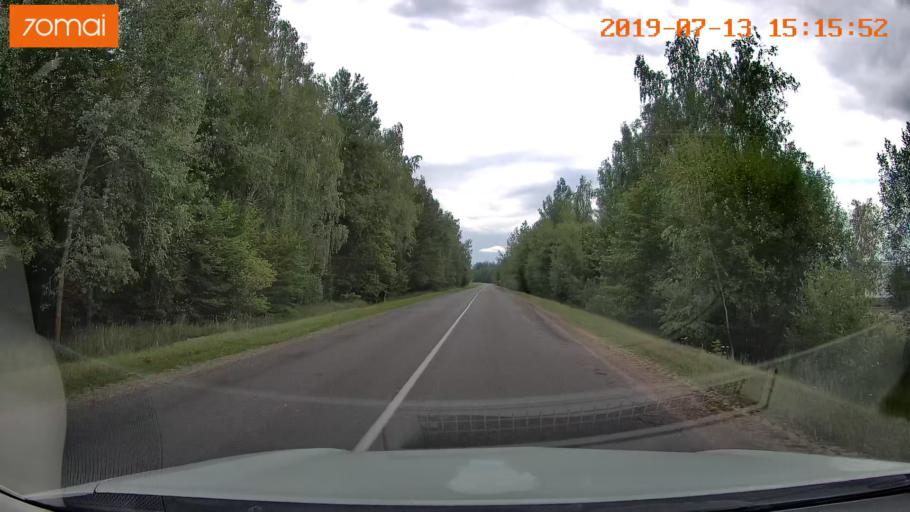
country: BY
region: Mogilev
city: Hlusha
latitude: 53.1139
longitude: 28.8289
